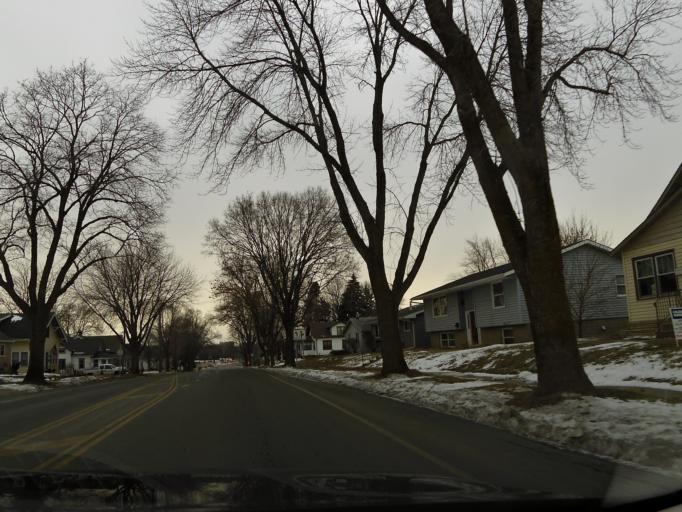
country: US
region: Minnesota
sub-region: Carver County
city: Waconia
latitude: 44.8456
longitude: -93.7877
